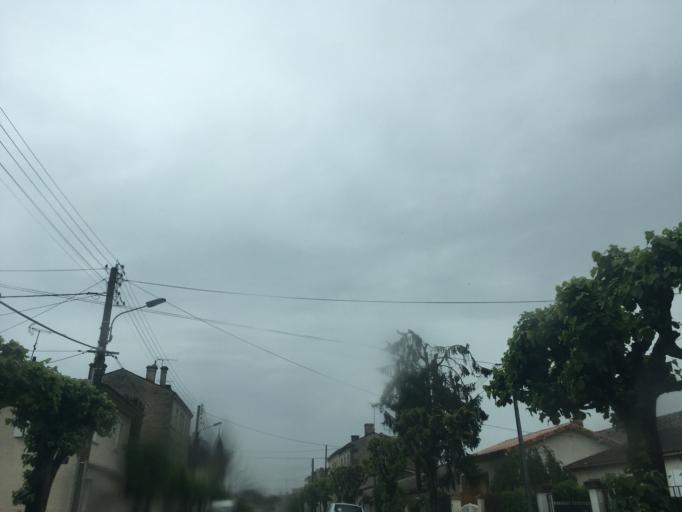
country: FR
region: Poitou-Charentes
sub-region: Departement de la Charente
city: Cognac
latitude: 45.6878
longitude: -0.3234
